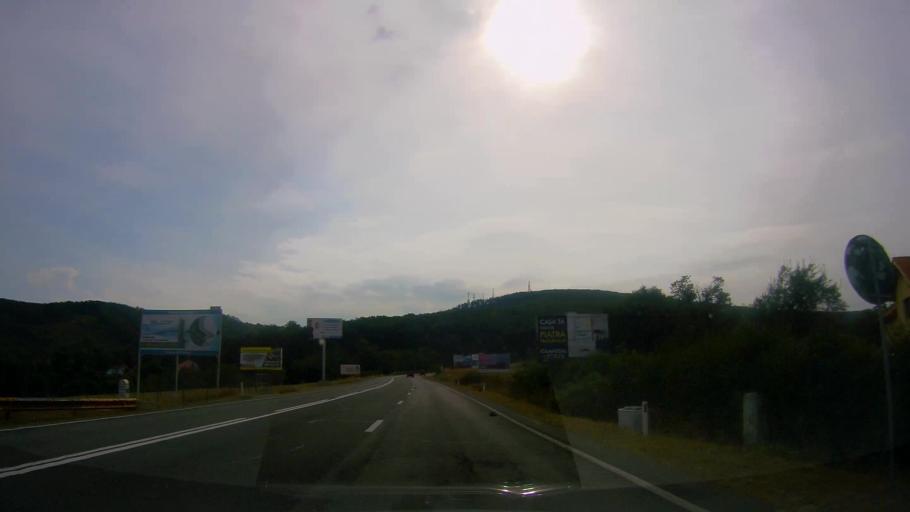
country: RO
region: Salaj
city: Zalau
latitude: 47.1619
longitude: 23.0860
